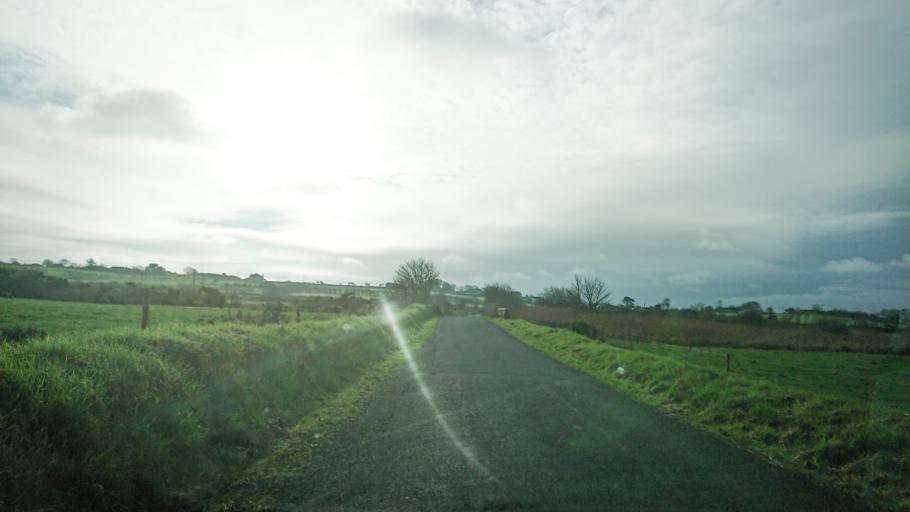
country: IE
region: Munster
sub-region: Waterford
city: Tra Mhor
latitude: 52.1614
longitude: -7.1880
